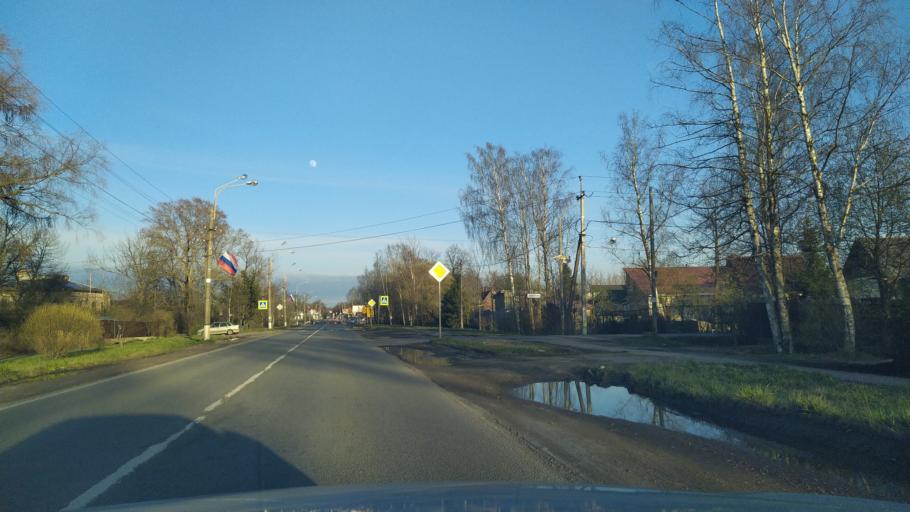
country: RU
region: St.-Petersburg
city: Aleksandrovskaya
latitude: 59.7351
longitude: 30.3362
